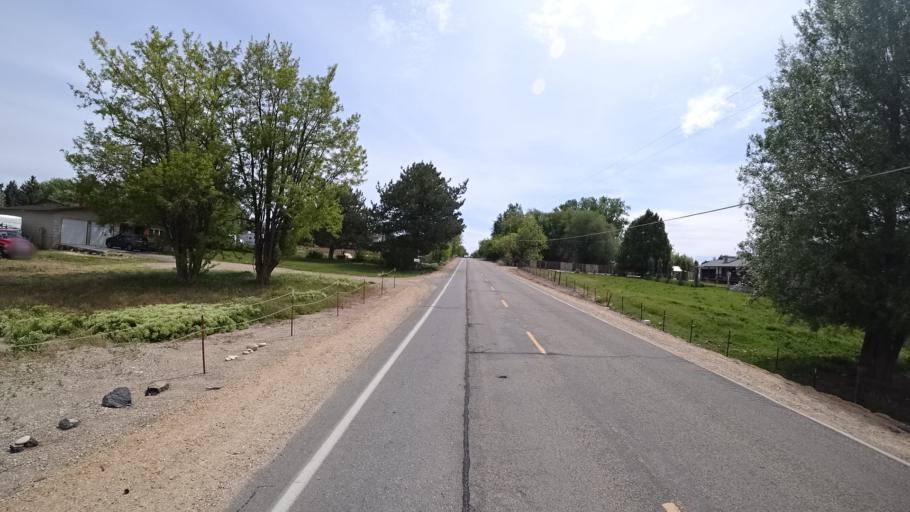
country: US
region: Idaho
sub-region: Ada County
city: Meridian
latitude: 43.5612
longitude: -116.3225
